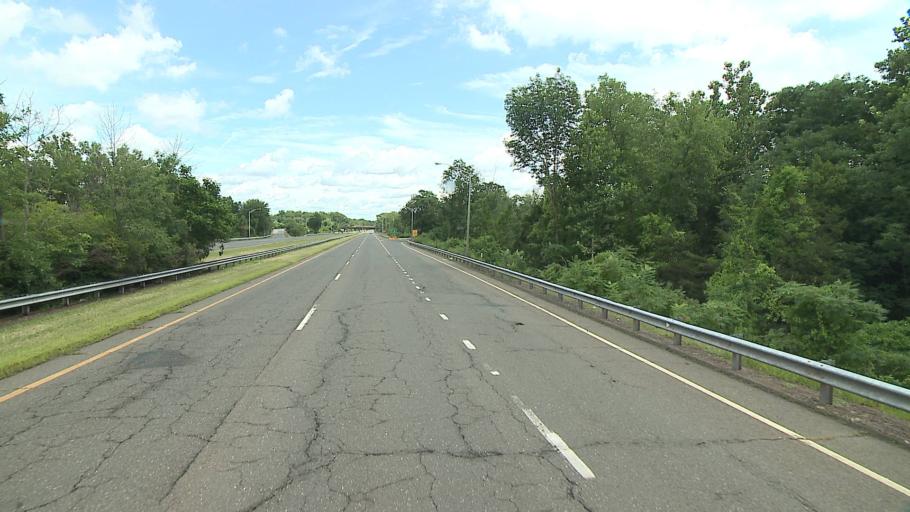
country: US
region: Connecticut
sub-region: Hartford County
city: Kensington
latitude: 41.6463
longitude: -72.7768
